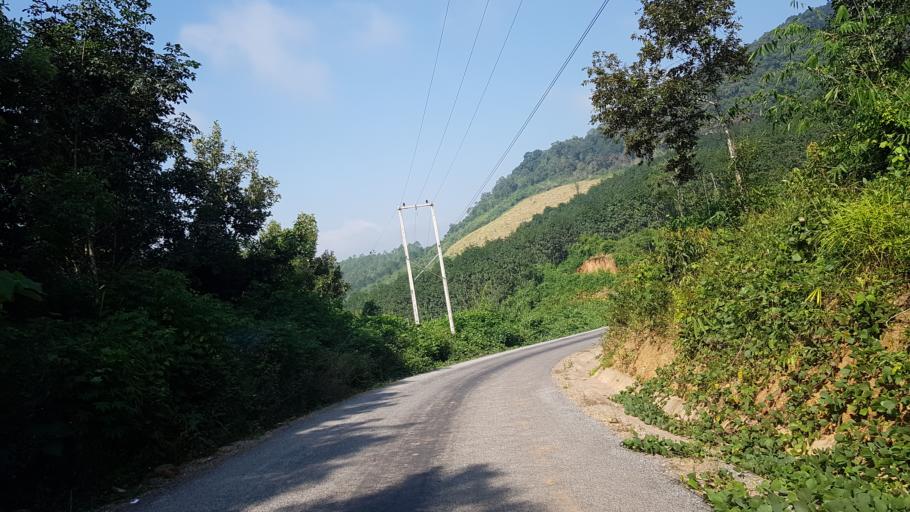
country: LA
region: Oudomxai
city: Muang Xay
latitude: 20.7132
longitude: 102.0673
